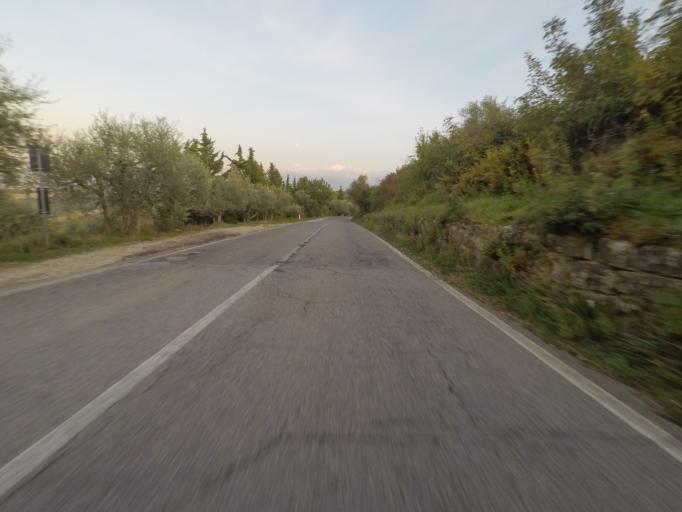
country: IT
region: Tuscany
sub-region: Provincia di Siena
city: Torrita di Siena
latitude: 43.1475
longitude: 11.7385
